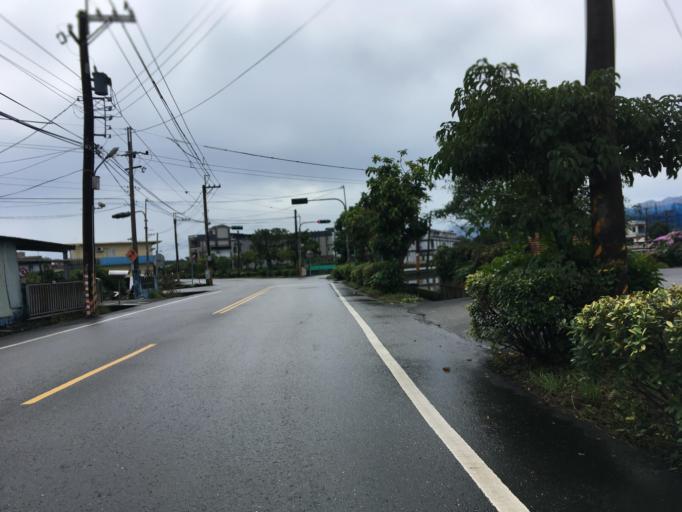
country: TW
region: Taiwan
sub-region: Yilan
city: Yilan
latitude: 24.6657
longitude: 121.7938
